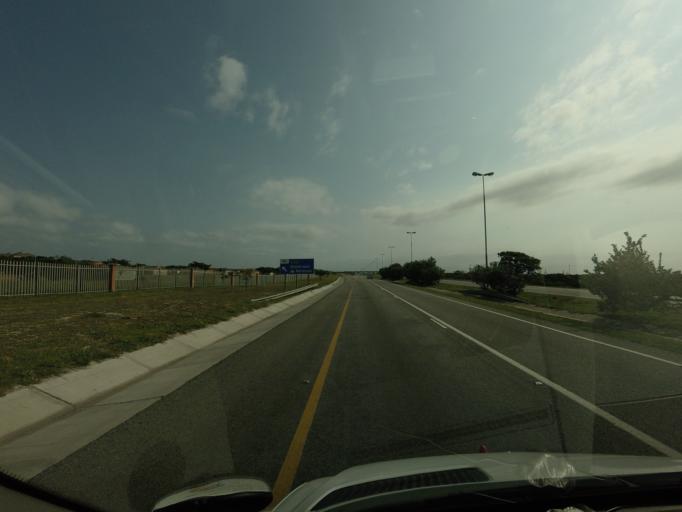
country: ZA
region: Eastern Cape
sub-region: Nelson Mandela Bay Metropolitan Municipality
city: Port Elizabeth
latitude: -33.8289
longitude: 25.6446
